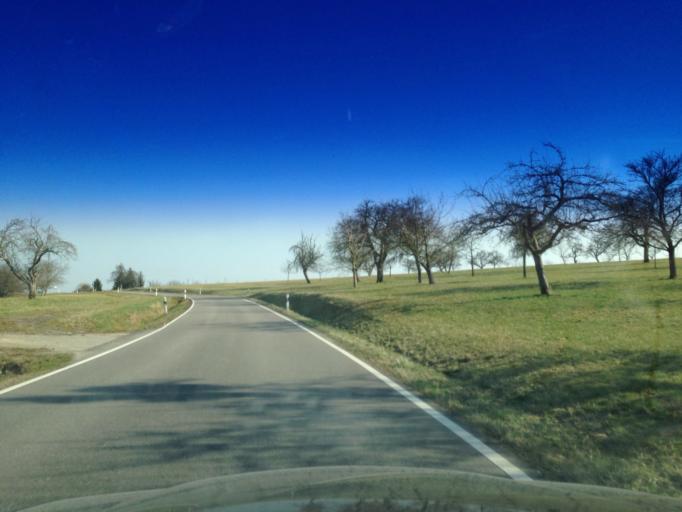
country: DE
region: Baden-Wuerttemberg
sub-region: Regierungsbezirk Stuttgart
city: Eberdingen
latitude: 48.8871
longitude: 8.9420
